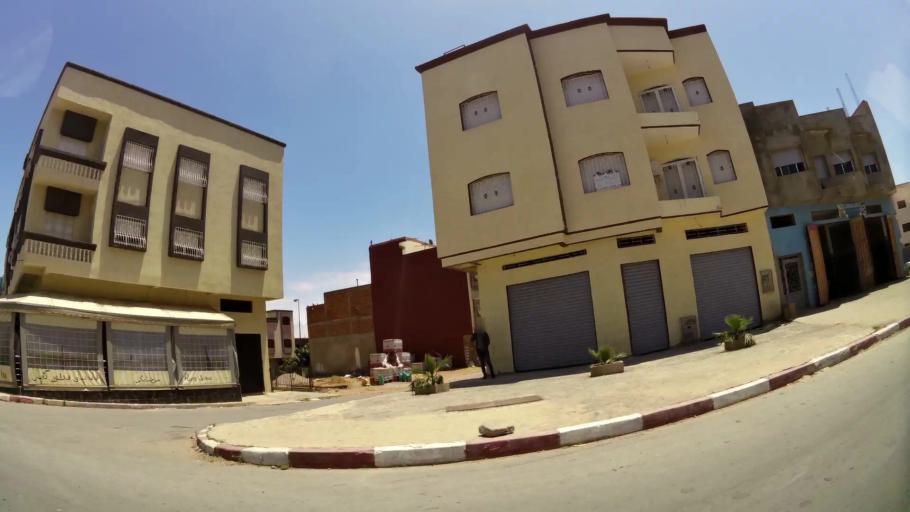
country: MA
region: Gharb-Chrarda-Beni Hssen
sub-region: Kenitra Province
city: Kenitra
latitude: 34.2595
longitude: -6.6481
